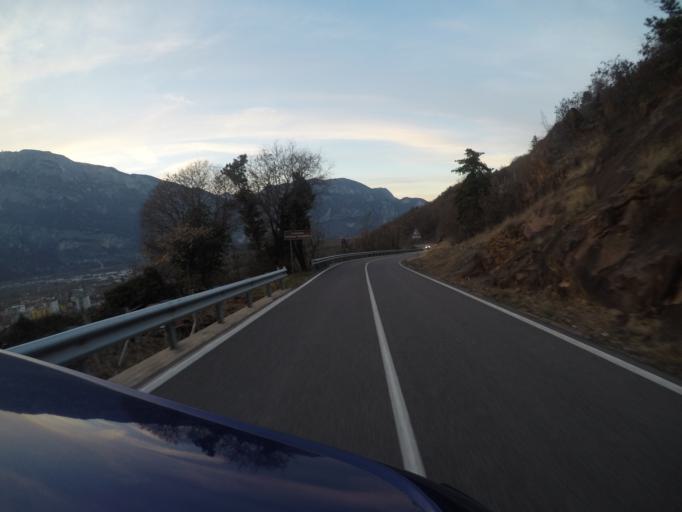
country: IT
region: Trentino-Alto Adige
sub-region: Provincia di Trento
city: Lavis
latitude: 46.1421
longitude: 11.1156
